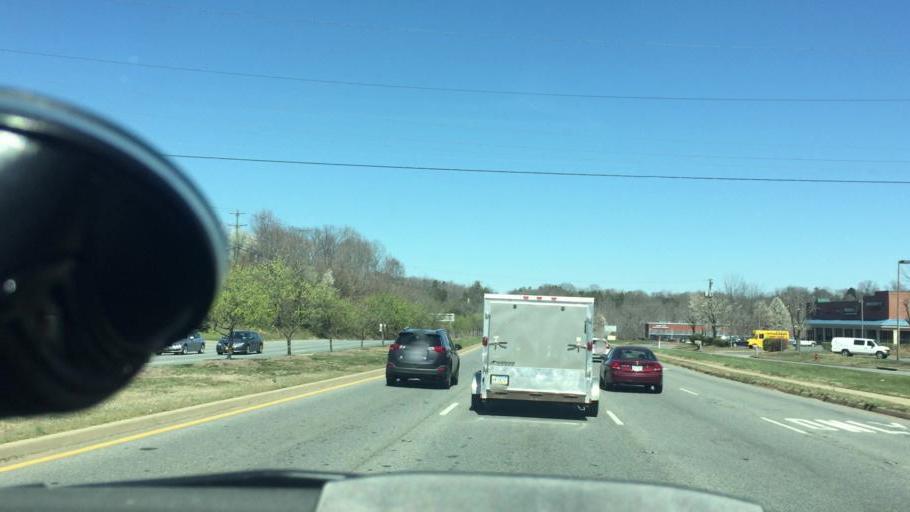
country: US
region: Virginia
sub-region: Albemarle County
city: Hollymead
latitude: 38.0980
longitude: -78.4637
